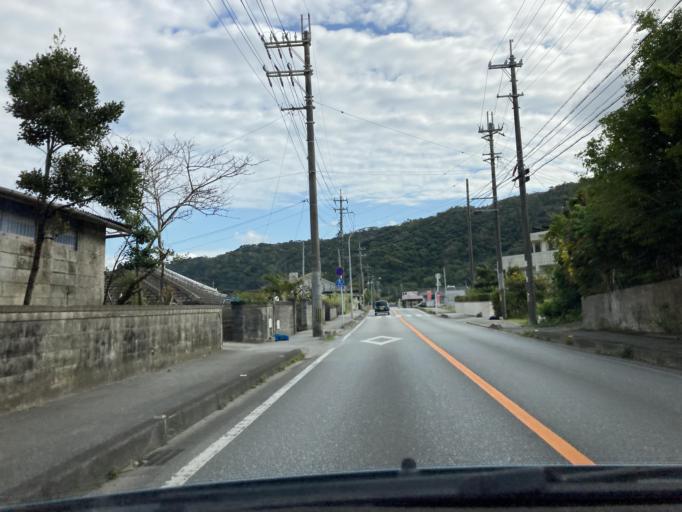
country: JP
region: Okinawa
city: Nago
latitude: 26.6519
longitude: 127.9813
